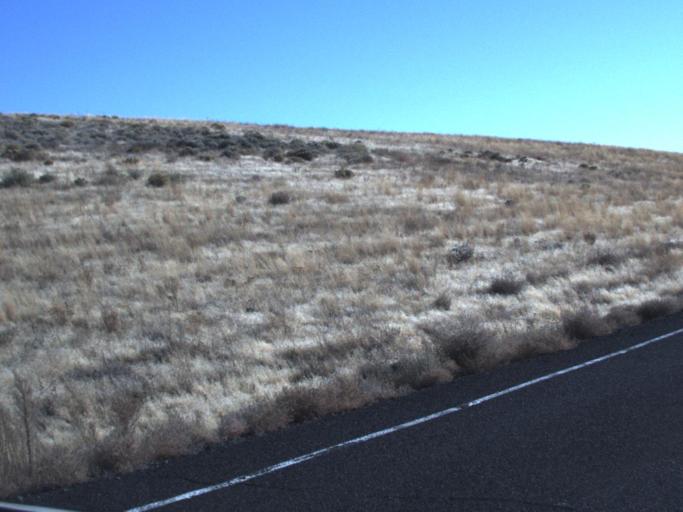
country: US
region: Washington
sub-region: Franklin County
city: Connell
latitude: 46.7049
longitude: -118.5278
